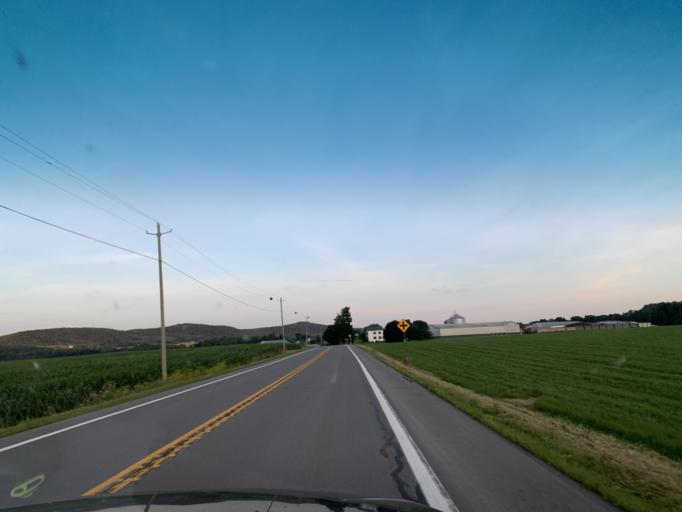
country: US
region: New York
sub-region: Oneida County
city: Chadwicks
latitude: 42.9196
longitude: -75.2449
